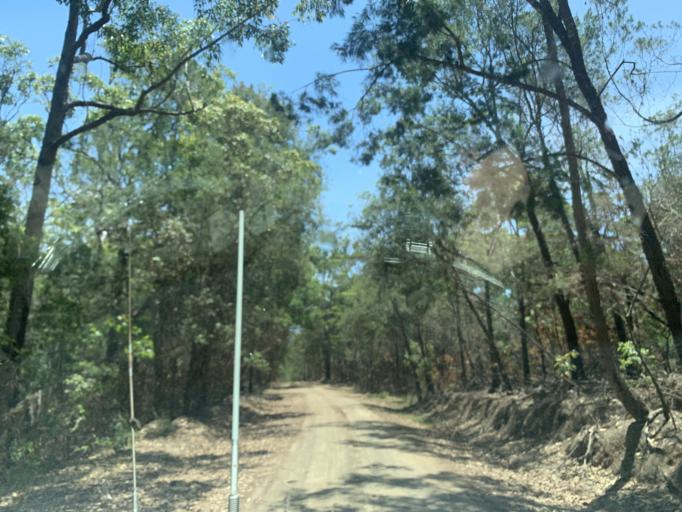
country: AU
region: Queensland
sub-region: Cairns
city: Redlynch
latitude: -16.9369
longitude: 145.6208
